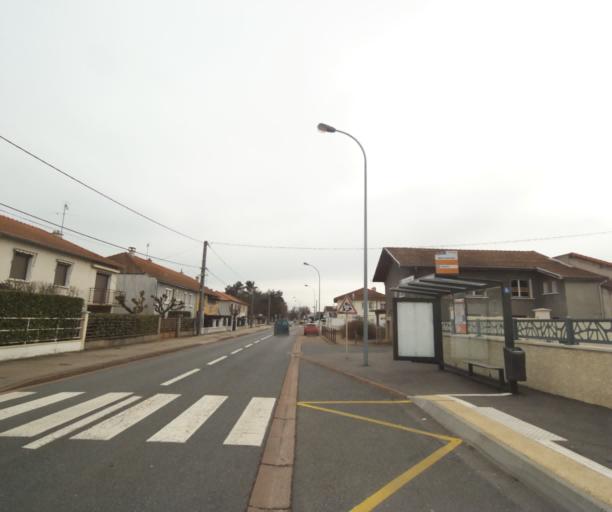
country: FR
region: Rhone-Alpes
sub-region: Departement de la Loire
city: Mably
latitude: 46.0682
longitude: 4.0739
